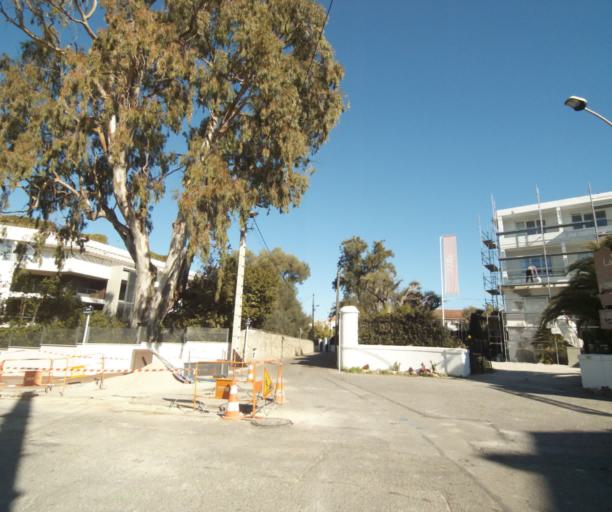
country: FR
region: Provence-Alpes-Cote d'Azur
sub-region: Departement des Alpes-Maritimes
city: Antibes
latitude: 43.5645
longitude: 7.1199
